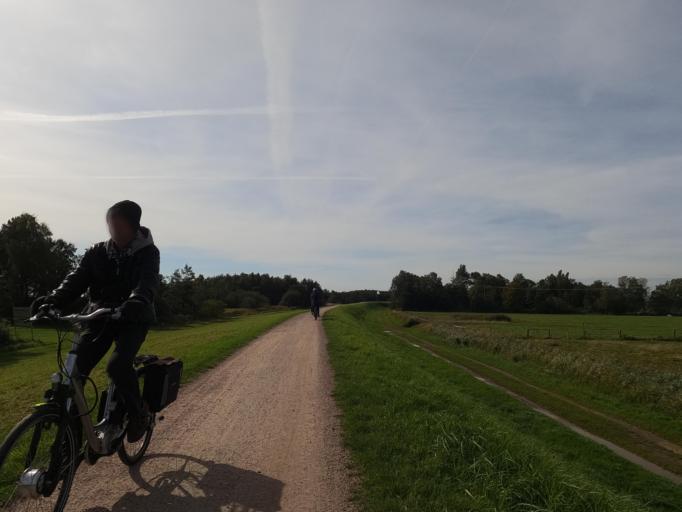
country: DE
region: Schleswig-Holstein
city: Kellenhusen
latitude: 54.1796
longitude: 11.0497
